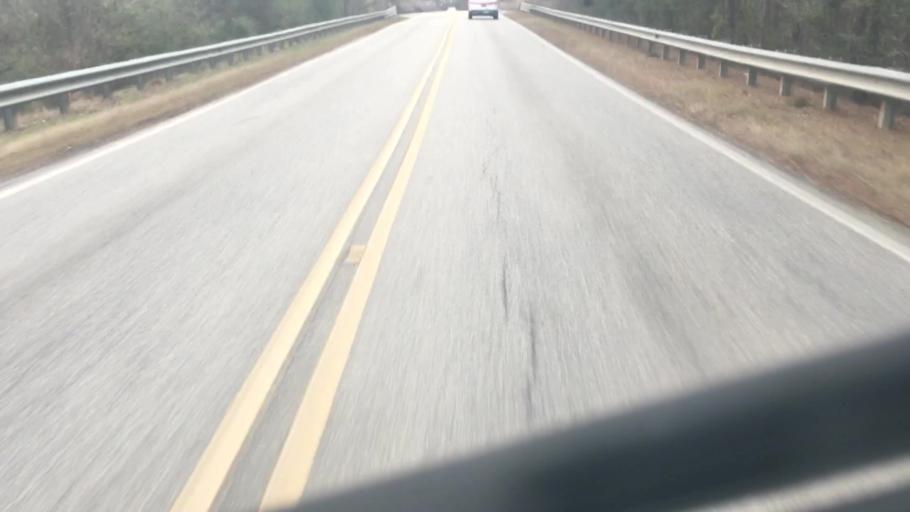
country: US
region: Alabama
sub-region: Jefferson County
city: Hoover
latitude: 33.3620
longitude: -86.8125
